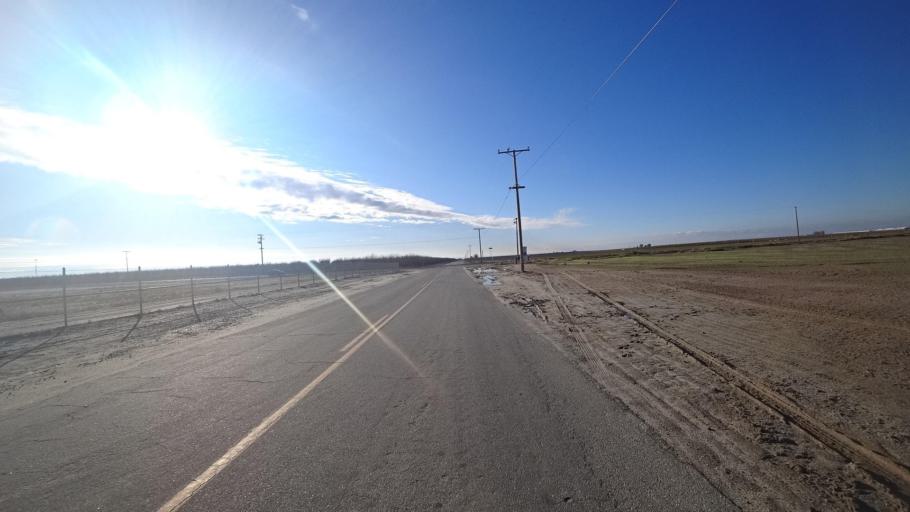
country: US
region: California
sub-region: Kern County
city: Delano
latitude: 35.7621
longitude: -119.3298
